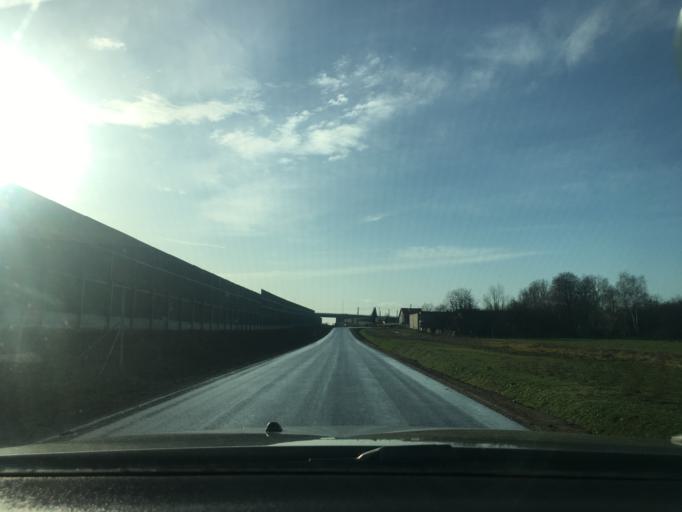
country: PL
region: Swietokrzyskie
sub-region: Powiat jedrzejowski
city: Jedrzejow
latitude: 50.6630
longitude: 20.3333
